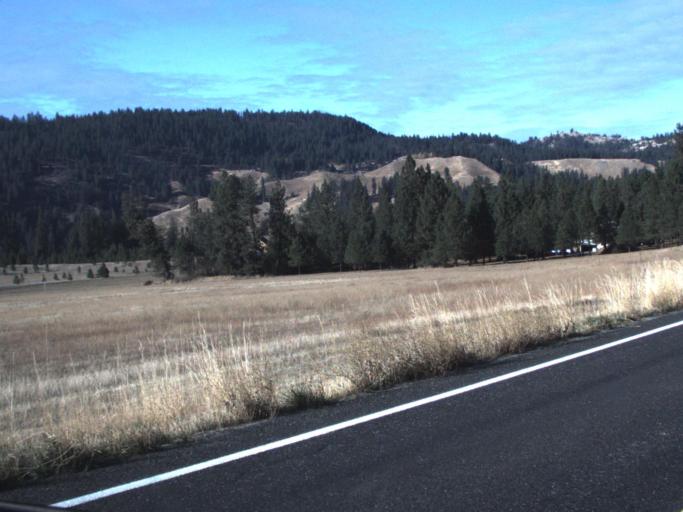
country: US
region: Washington
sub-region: Stevens County
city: Kettle Falls
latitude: 48.2062
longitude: -118.1798
